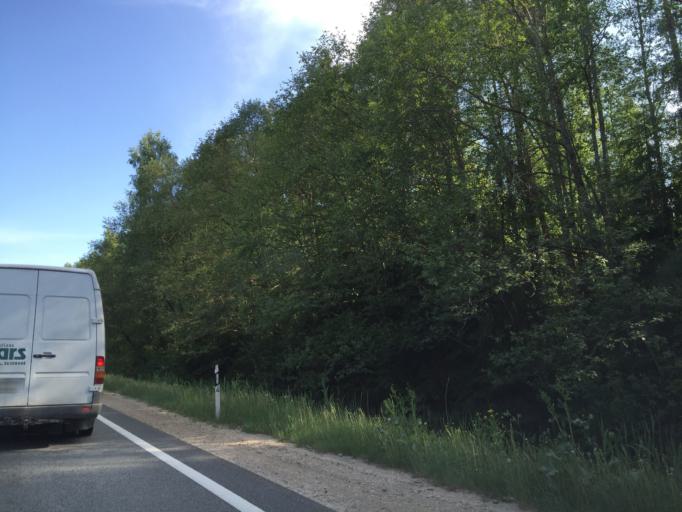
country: LV
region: Salaspils
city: Salaspils
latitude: 56.9169
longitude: 24.3988
